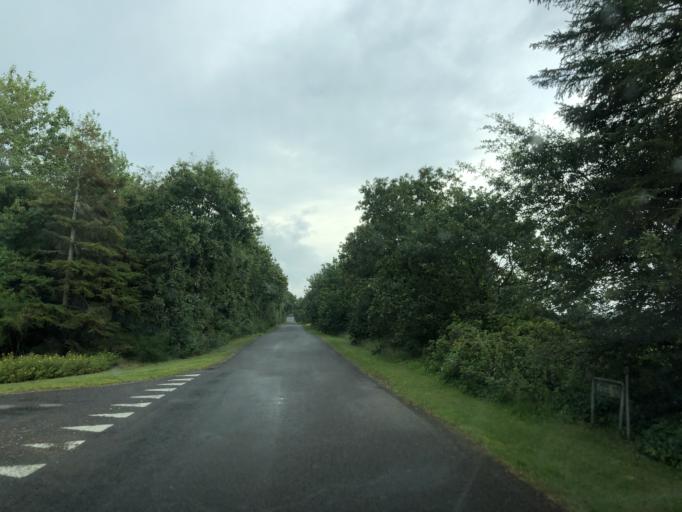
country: DK
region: Central Jutland
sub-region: Ringkobing-Skjern Kommune
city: Skjern
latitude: 55.8861
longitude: 8.4241
